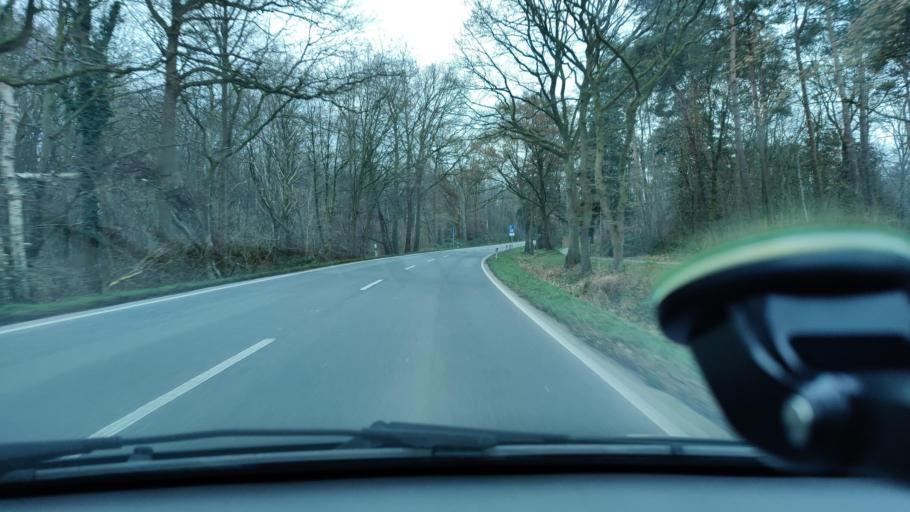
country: DE
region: North Rhine-Westphalia
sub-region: Regierungsbezirk Dusseldorf
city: Sonsbeck
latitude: 51.5946
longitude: 6.3853
